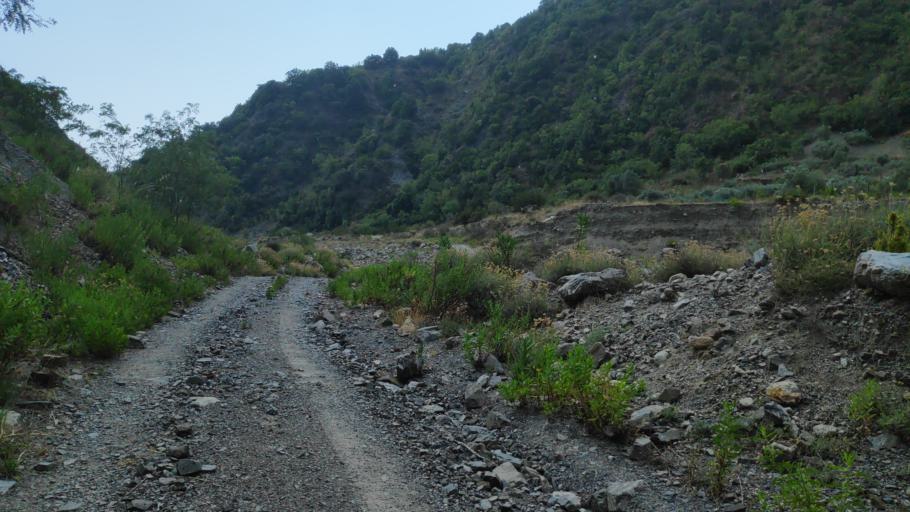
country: IT
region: Calabria
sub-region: Provincia di Reggio Calabria
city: Bivongi
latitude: 38.4942
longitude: 16.4490
